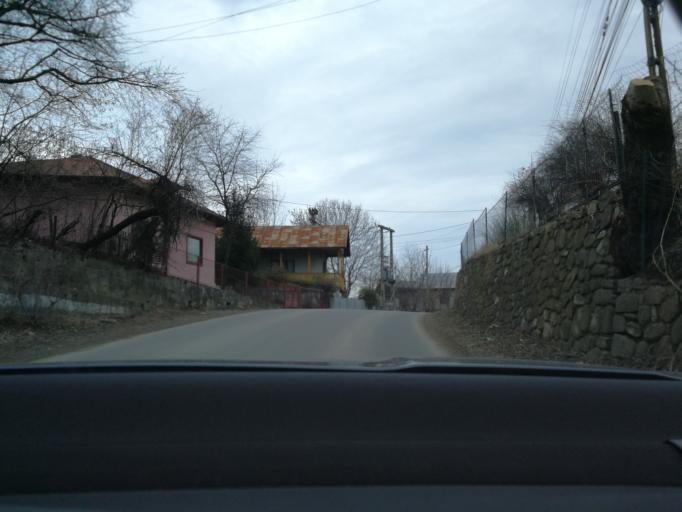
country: RO
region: Prahova
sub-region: Comuna Telega
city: Telega
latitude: 45.1411
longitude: 25.7784
